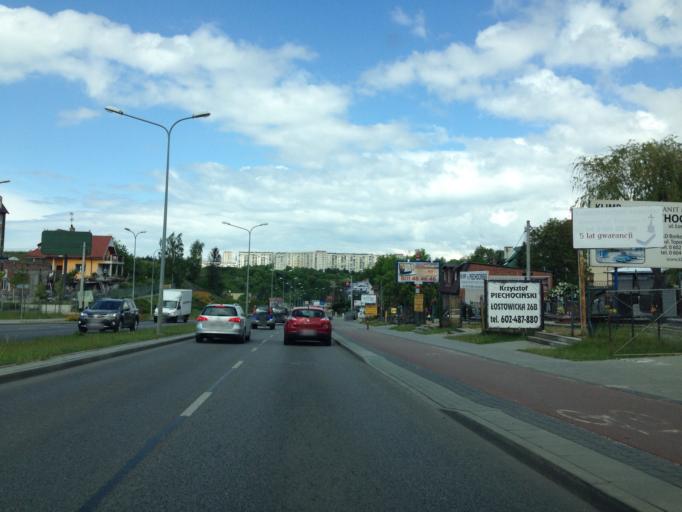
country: PL
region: Pomeranian Voivodeship
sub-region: Gdansk
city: Gdansk
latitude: 54.3427
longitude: 18.6019
